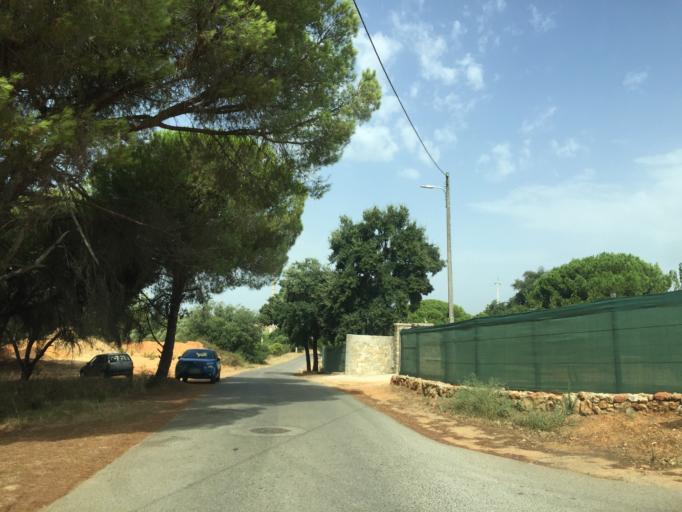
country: PT
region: Faro
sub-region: Loule
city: Vilamoura
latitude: 37.1037
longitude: -8.1015
